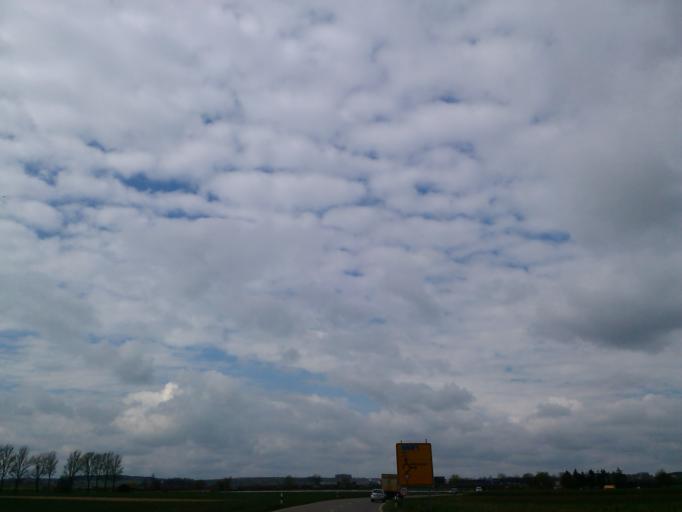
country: DE
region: Baden-Wuerttemberg
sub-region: Tuebingen Region
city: Langenau
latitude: 48.4927
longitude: 10.1042
